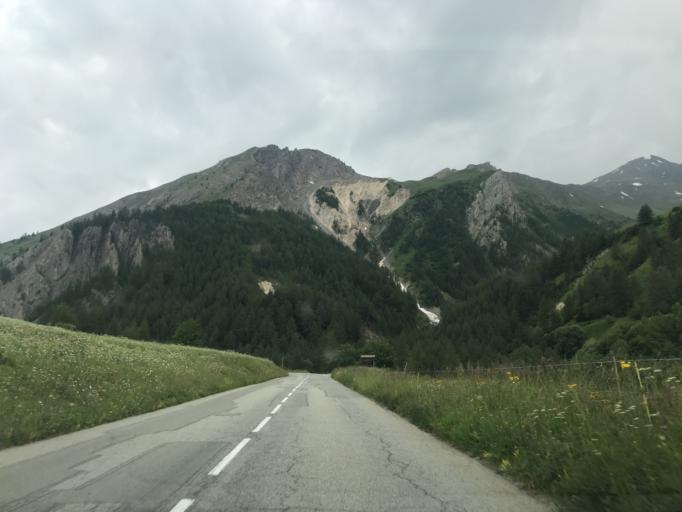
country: FR
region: Rhone-Alpes
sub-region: Departement de la Savoie
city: Valloire
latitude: 45.1233
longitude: 6.4185
